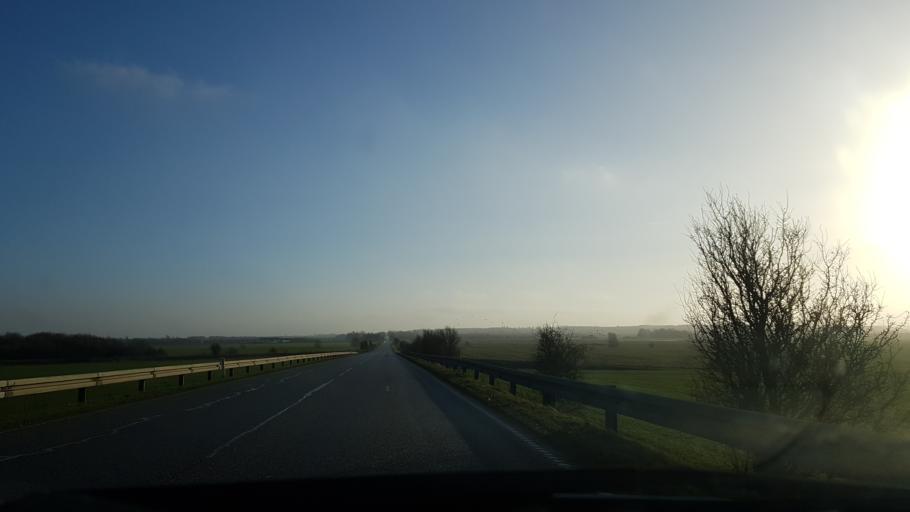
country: DK
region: South Denmark
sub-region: Tonder Kommune
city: Toftlund
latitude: 55.2481
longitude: 9.1517
